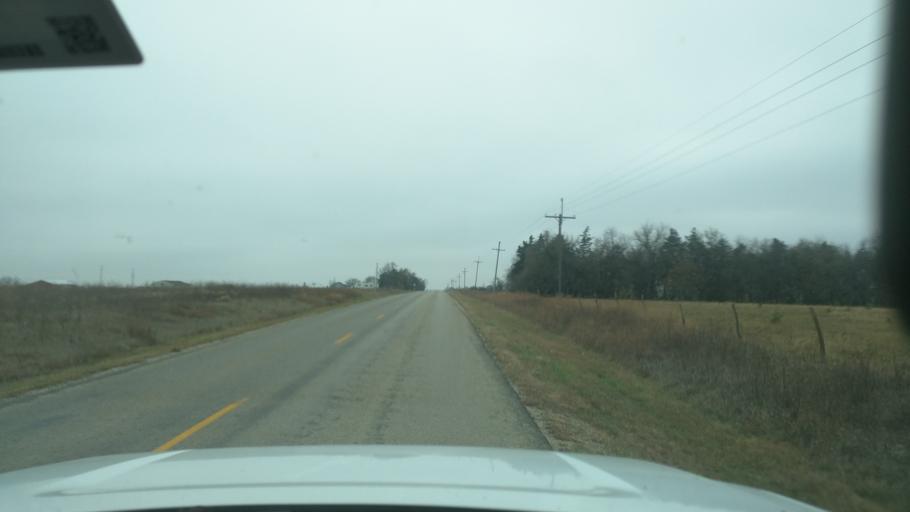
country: US
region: Kansas
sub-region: Lyon County
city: Emporia
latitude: 38.5561
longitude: -96.2612
